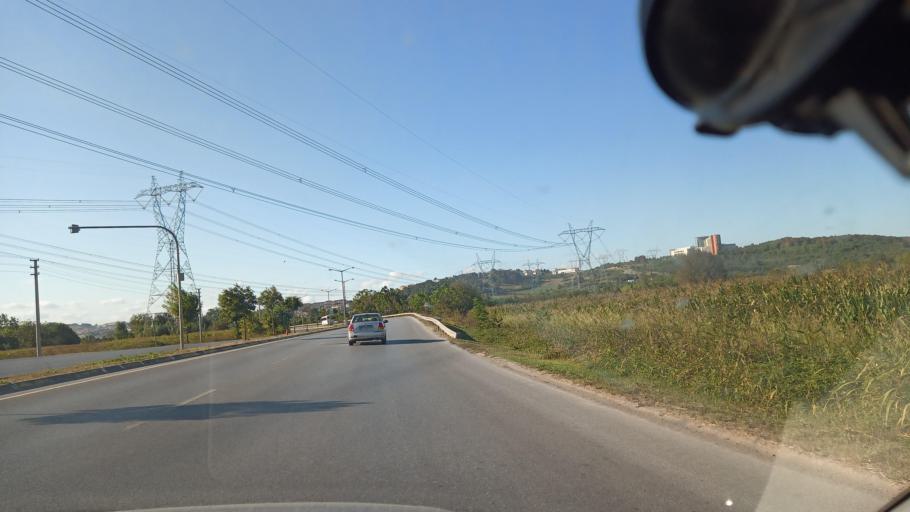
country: TR
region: Sakarya
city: Kazimpasa
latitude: 40.8364
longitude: 30.3454
